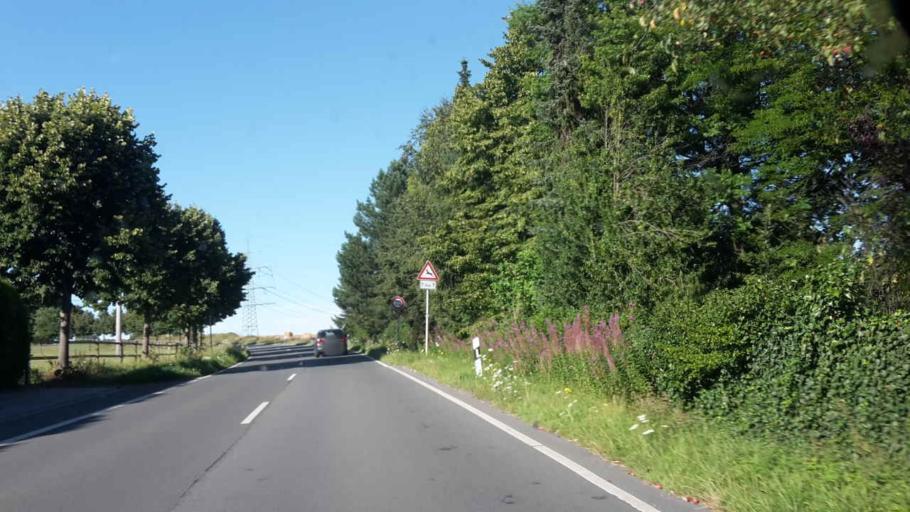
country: DE
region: North Rhine-Westphalia
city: Schwerte
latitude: 51.4572
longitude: 7.6018
